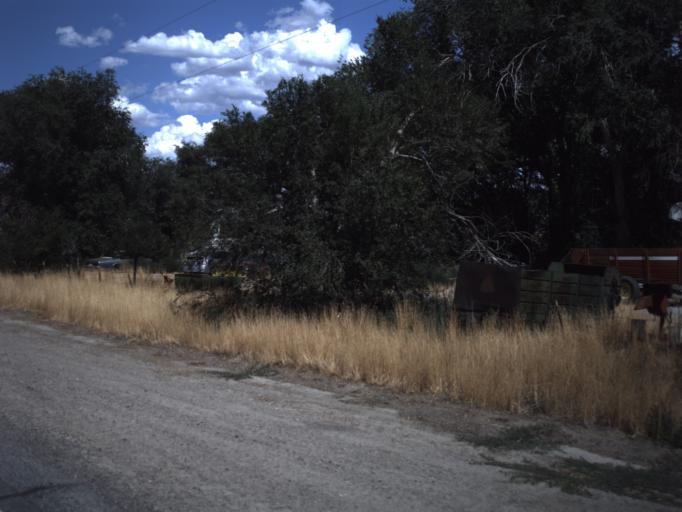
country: US
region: Utah
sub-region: Millard County
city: Delta
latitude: 39.5395
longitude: -112.3637
